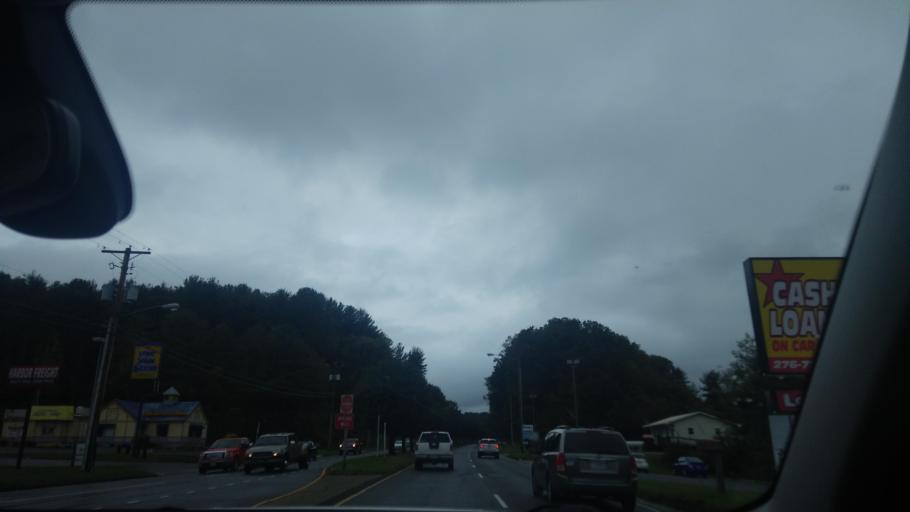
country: US
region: Virginia
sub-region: City of Galax
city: Galax
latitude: 36.6792
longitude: -80.8974
